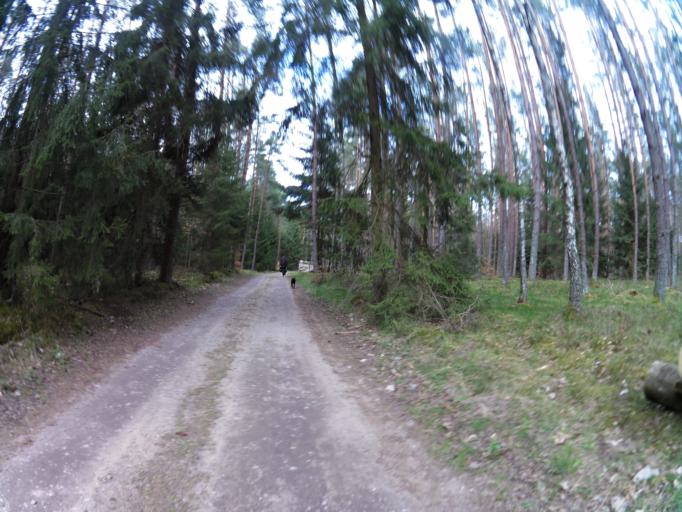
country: PL
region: West Pomeranian Voivodeship
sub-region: Powiat szczecinecki
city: Szczecinek
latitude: 53.8312
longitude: 16.6574
